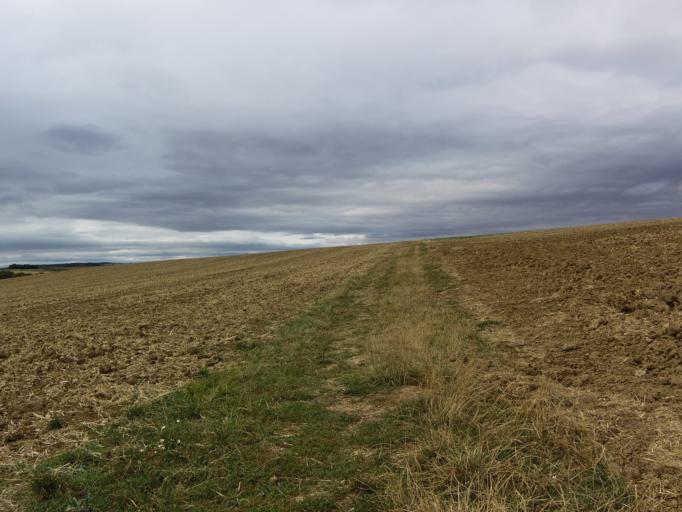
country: DE
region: Bavaria
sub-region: Regierungsbezirk Unterfranken
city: Rimpar
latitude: 49.8423
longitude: 9.9660
